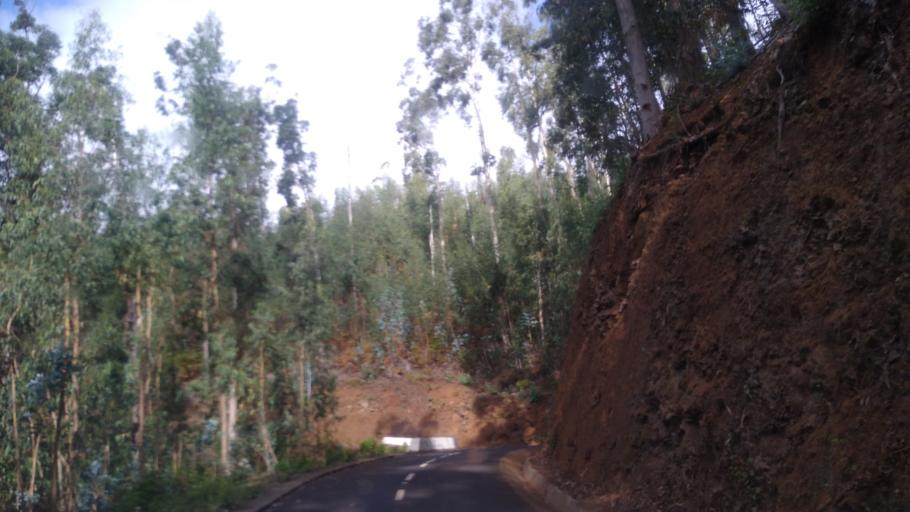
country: PT
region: Madeira
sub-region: Camara de Lobos
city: Curral das Freiras
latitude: 32.6955
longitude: -16.9412
